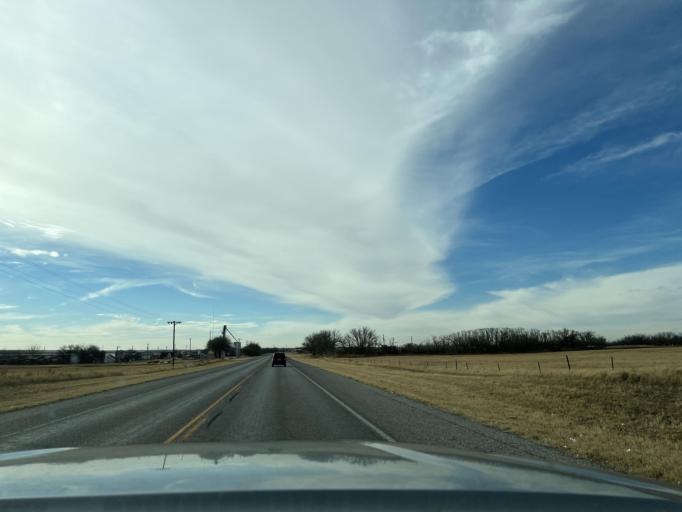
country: US
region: Texas
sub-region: Fisher County
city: Roby
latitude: 32.7542
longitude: -100.2563
